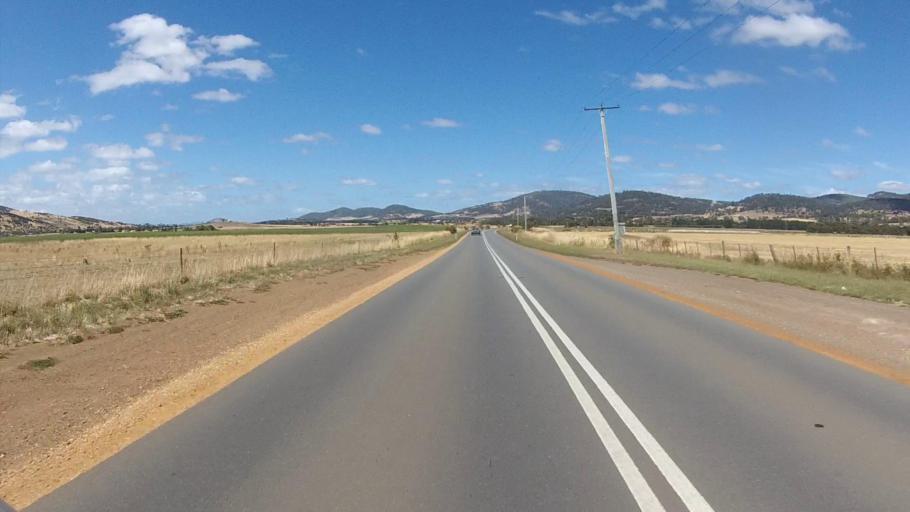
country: AU
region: Tasmania
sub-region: Clarence
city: Cambridge
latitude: -42.7570
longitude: 147.4156
